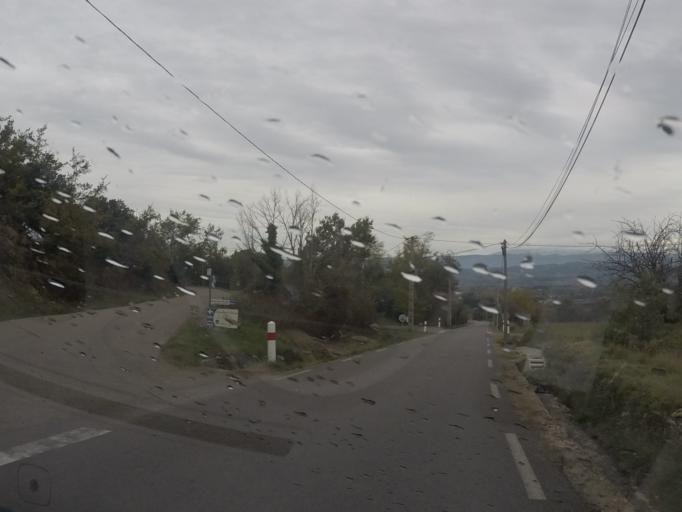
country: FR
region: Provence-Alpes-Cote d'Azur
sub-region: Departement du Vaucluse
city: Bonnieux
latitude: 43.8323
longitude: 5.2954
